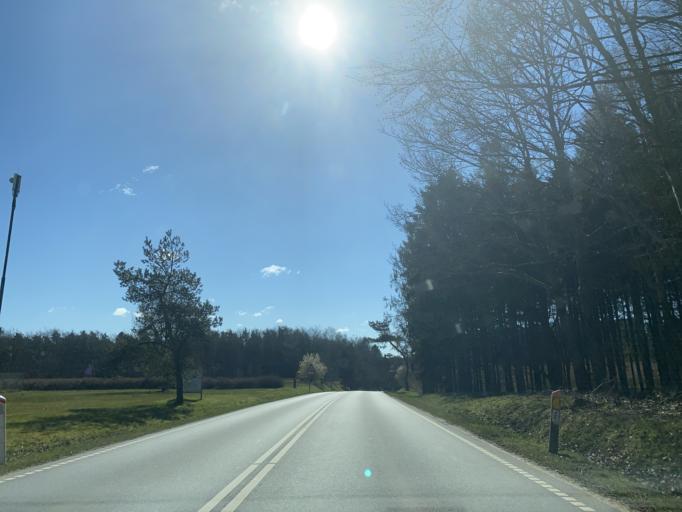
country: DK
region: Central Jutland
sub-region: Viborg Kommune
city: Bjerringbro
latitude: 56.2697
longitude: 9.6198
